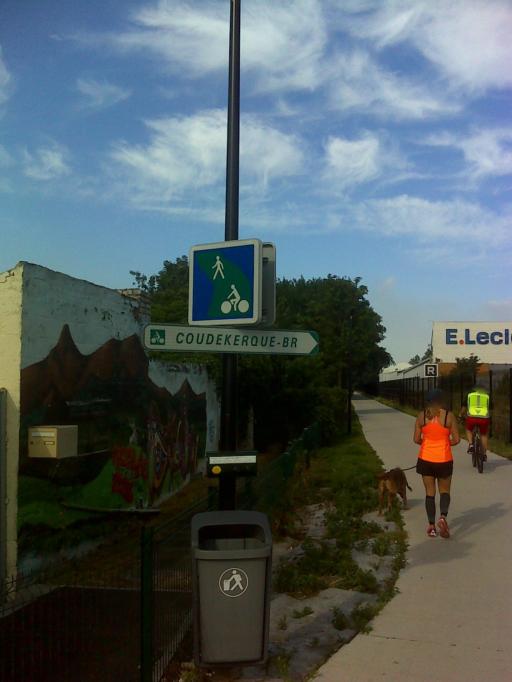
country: FR
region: Nord-Pas-de-Calais
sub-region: Departement du Nord
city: Coudekerque-Branche
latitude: 51.0465
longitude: 2.4185
